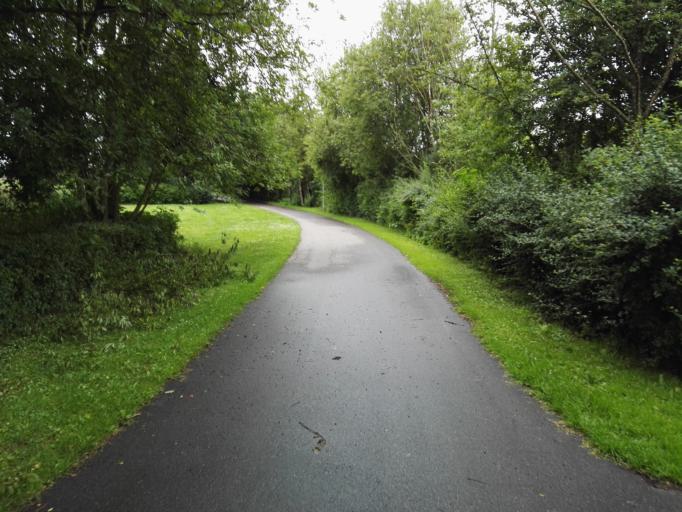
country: DK
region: Capital Region
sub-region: Egedal Kommune
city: Olstykke
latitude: 55.7720
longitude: 12.1634
